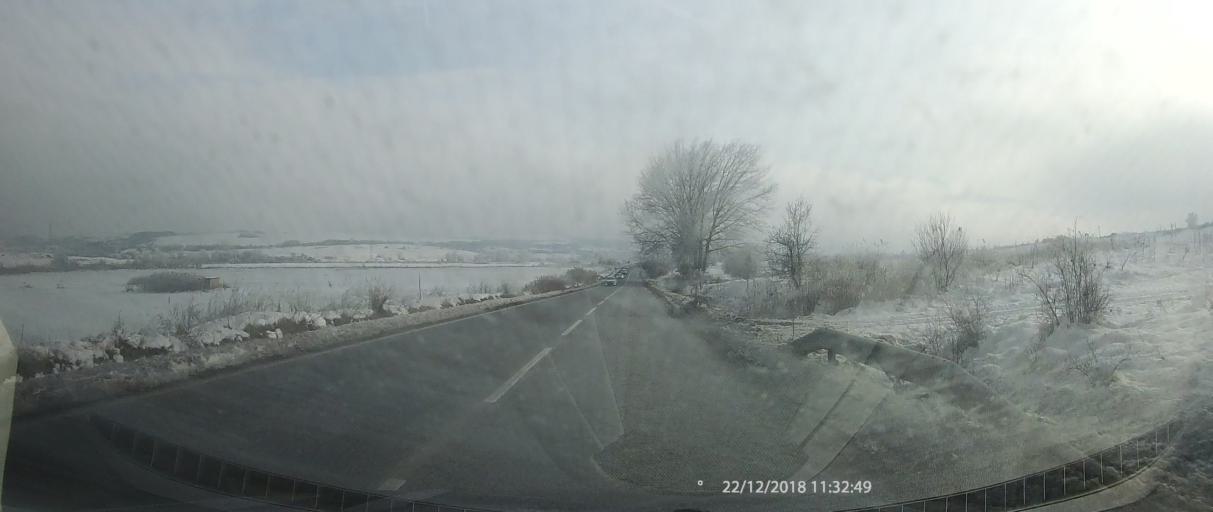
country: BG
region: Kyustendil
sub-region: Obshtina Dupnitsa
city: Dupnitsa
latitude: 42.2719
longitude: 23.0331
